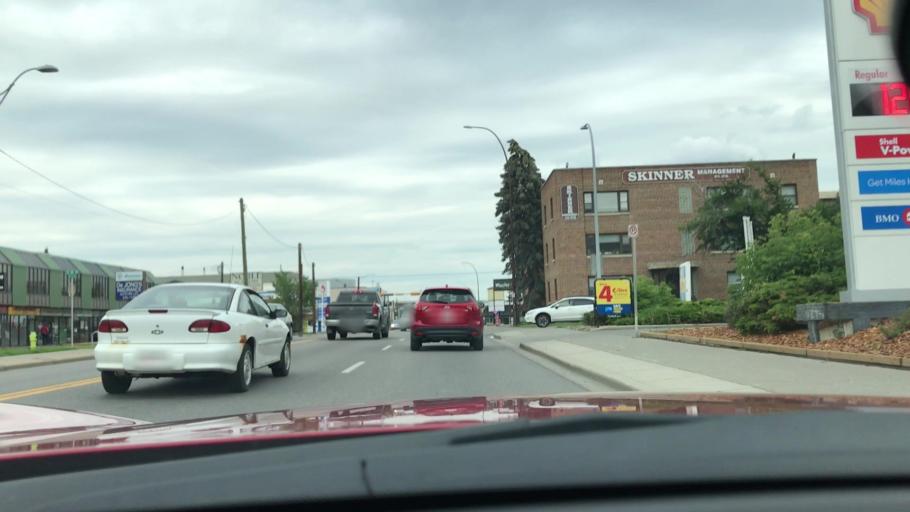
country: CA
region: Alberta
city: Calgary
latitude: 51.0409
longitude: -114.0947
